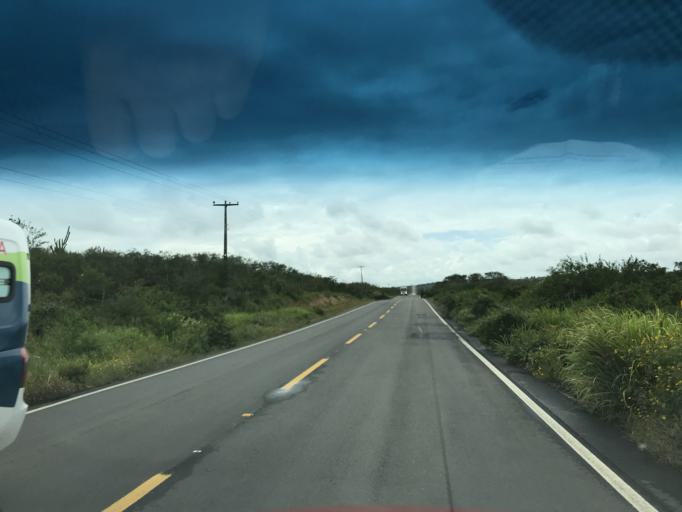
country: BR
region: Bahia
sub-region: Castro Alves
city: Castro Alves
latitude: -12.6789
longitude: -39.3008
